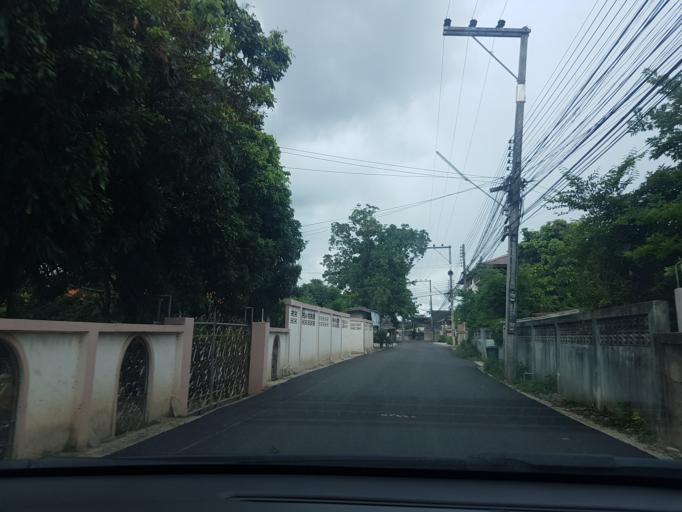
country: TH
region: Lampang
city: Ko Kha
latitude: 18.2292
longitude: 99.4205
